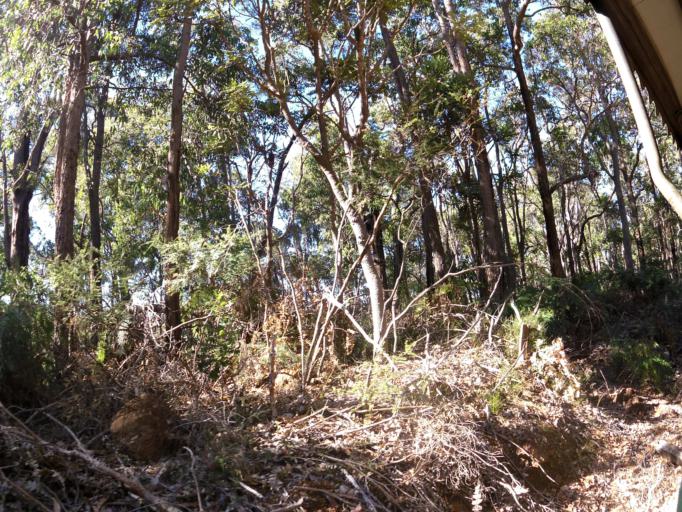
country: AU
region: Western Australia
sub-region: Waroona
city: Waroona
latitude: -32.7091
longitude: 116.0692
